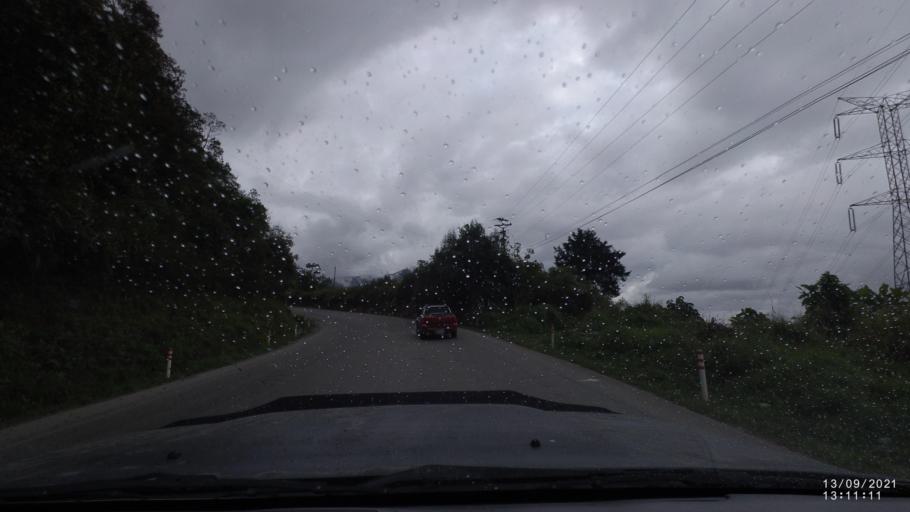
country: BO
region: Cochabamba
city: Colomi
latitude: -17.2033
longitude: -65.8291
